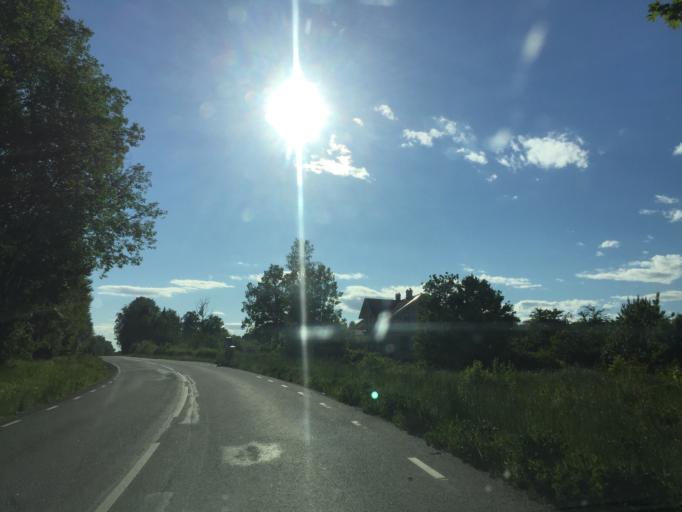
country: SE
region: OErebro
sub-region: Hallsbergs Kommun
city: Skollersta
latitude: 59.2026
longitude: 15.2928
